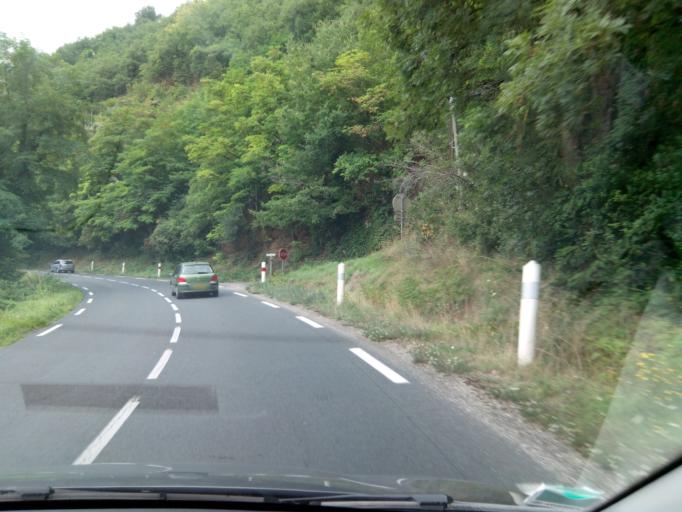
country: FR
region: Midi-Pyrenees
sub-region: Departement du Lot
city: Souillac
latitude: 44.8914
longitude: 1.4400
